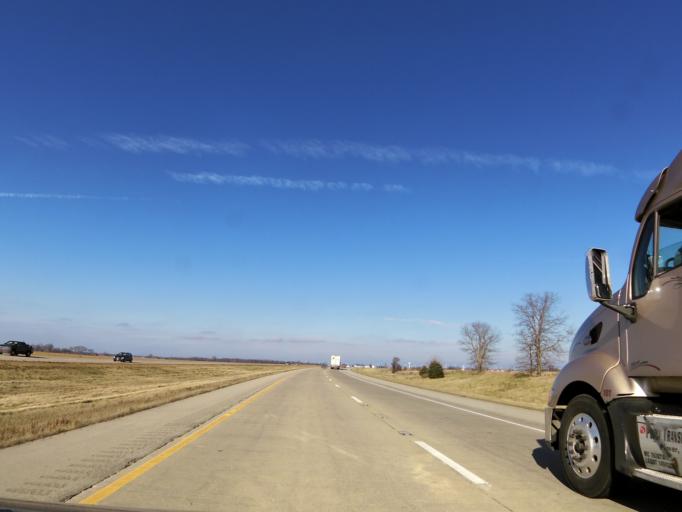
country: US
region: Illinois
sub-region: LaSalle County
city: Mendota
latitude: 41.5176
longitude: -89.0559
